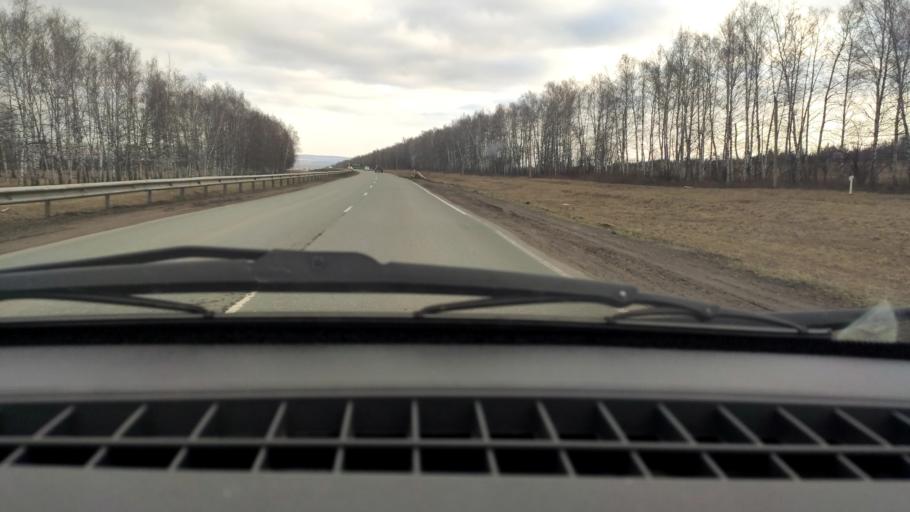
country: RU
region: Bashkortostan
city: Chishmy
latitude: 54.6247
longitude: 55.3764
